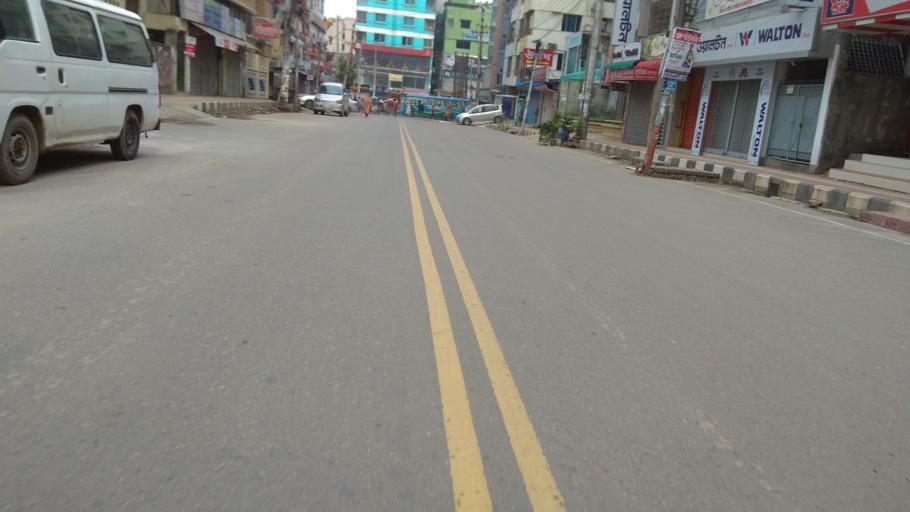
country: BD
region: Dhaka
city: Azimpur
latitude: 23.8097
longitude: 90.3689
